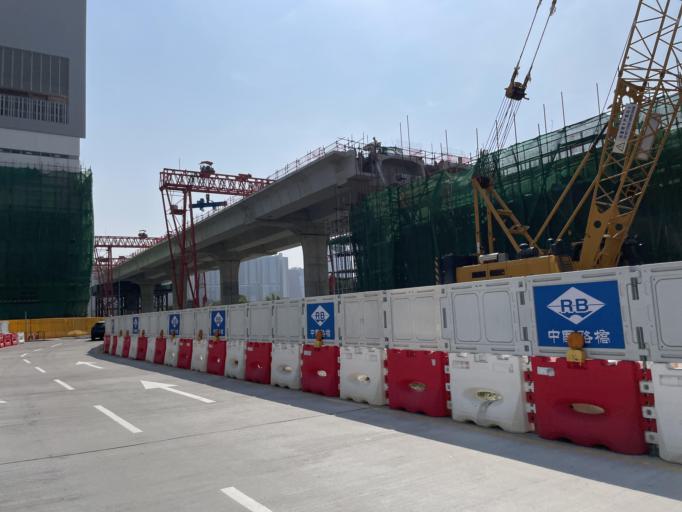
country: MO
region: Macau
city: Macau
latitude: 22.1375
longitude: 113.5639
